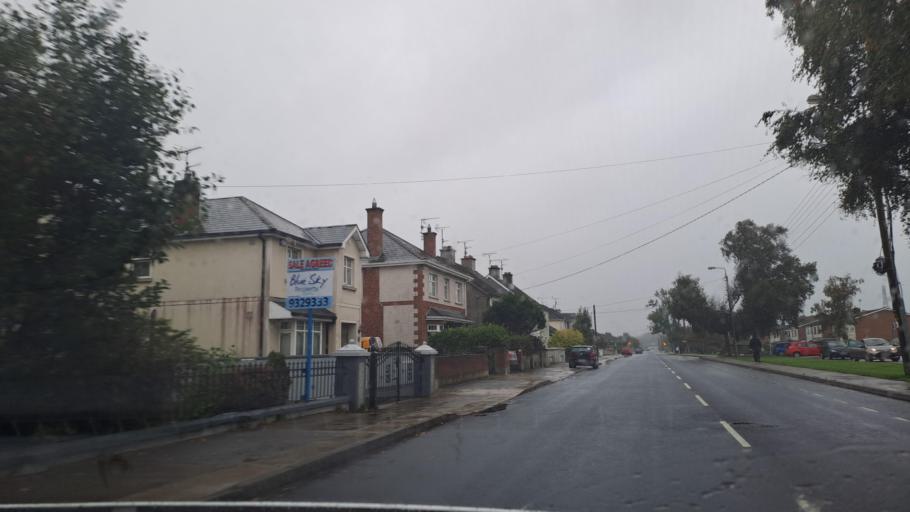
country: IE
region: Leinster
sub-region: Lu
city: Dundalk
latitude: 53.9955
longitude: -6.3953
